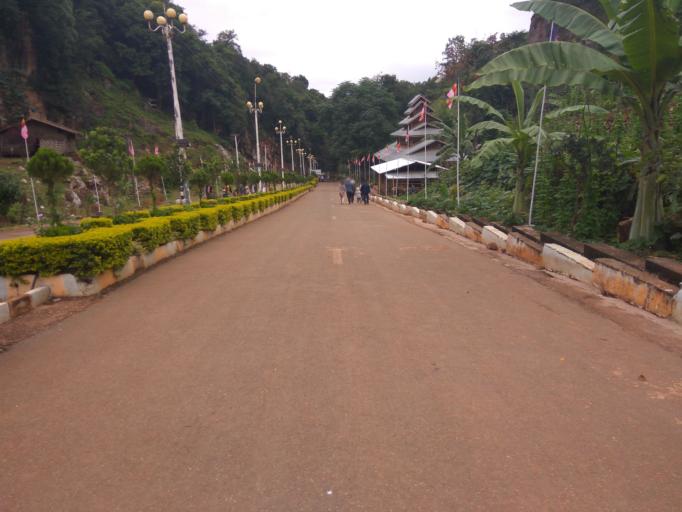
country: MM
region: Shan
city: Taunggyi
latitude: 20.8177
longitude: 97.3351
